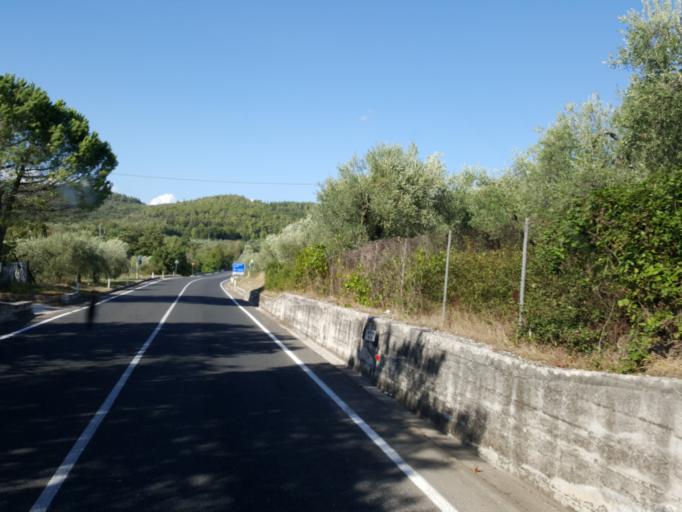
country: IT
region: Molise
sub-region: Provincia di Isernia
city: Macchia d'Isernia
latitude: 41.5450
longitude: 14.1594
